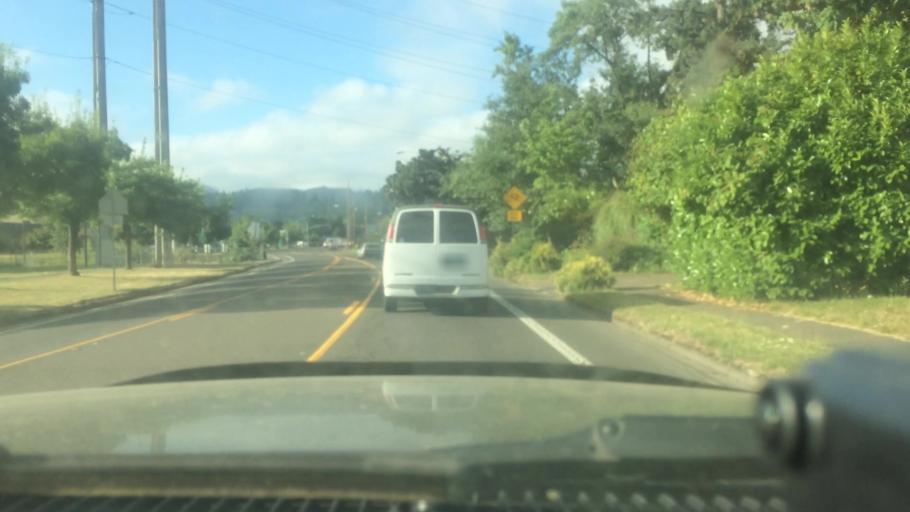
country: US
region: Oregon
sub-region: Lane County
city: Eugene
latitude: 44.0430
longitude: -123.1182
